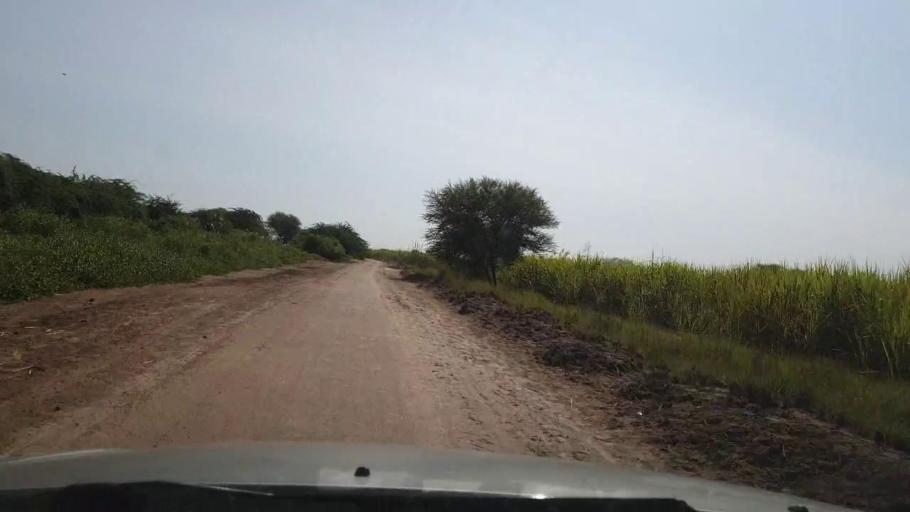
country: PK
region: Sindh
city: Bulri
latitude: 25.0122
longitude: 68.3200
